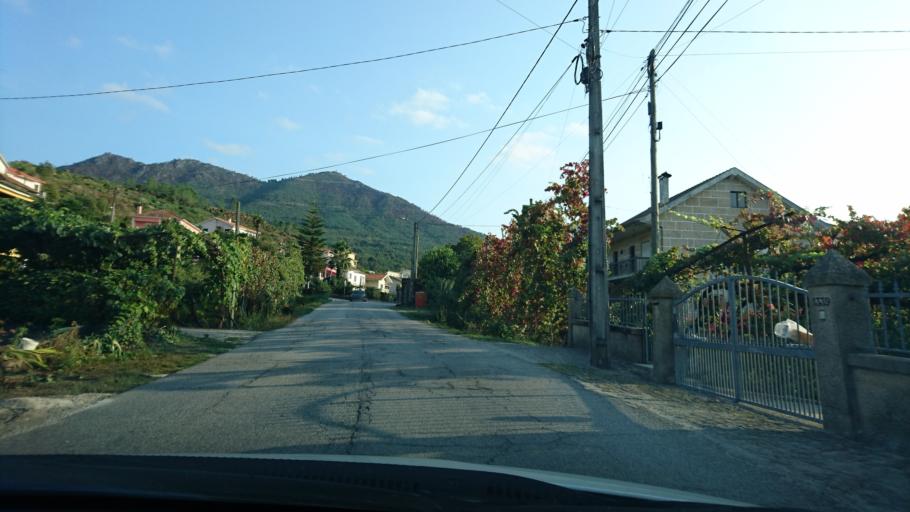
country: PT
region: Vila Real
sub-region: Mondim de Basto
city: Mondim de Basto
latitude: 41.4386
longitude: -7.9268
